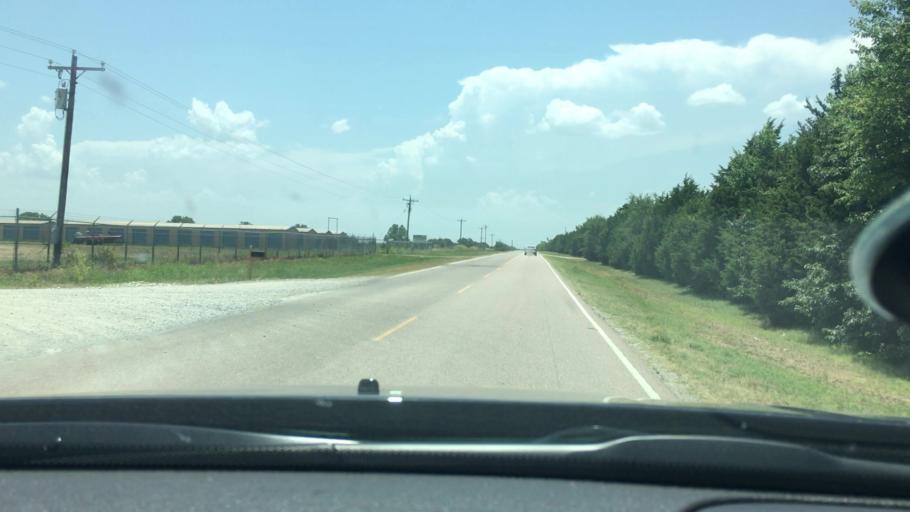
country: US
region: Oklahoma
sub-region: Johnston County
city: Tishomingo
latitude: 34.2829
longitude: -96.6711
